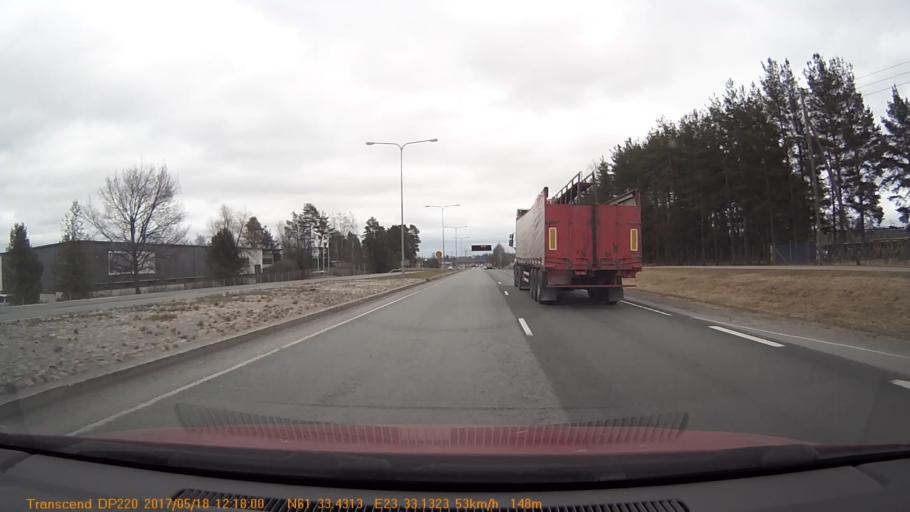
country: FI
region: Pirkanmaa
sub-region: Tampere
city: Yloejaervi
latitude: 61.5572
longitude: 23.5522
